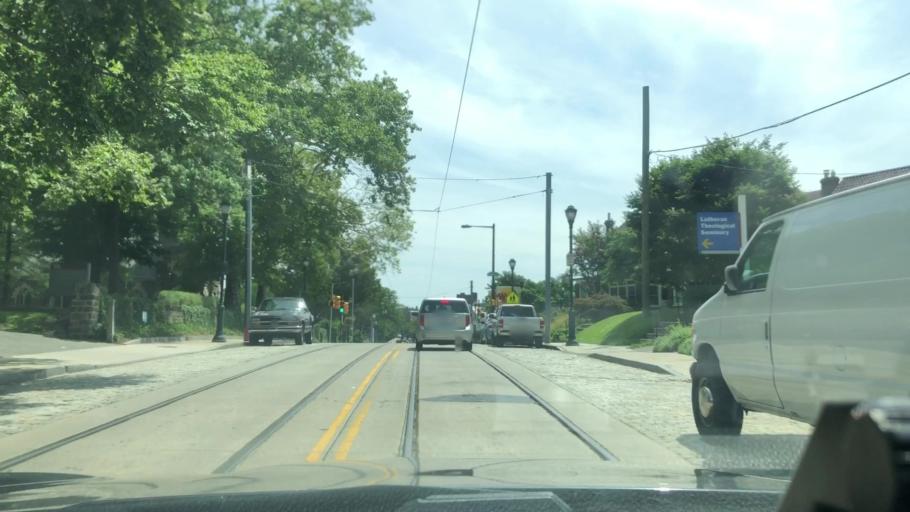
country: US
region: Pennsylvania
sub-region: Montgomery County
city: Wyndmoor
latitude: 40.0618
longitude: -75.1924
